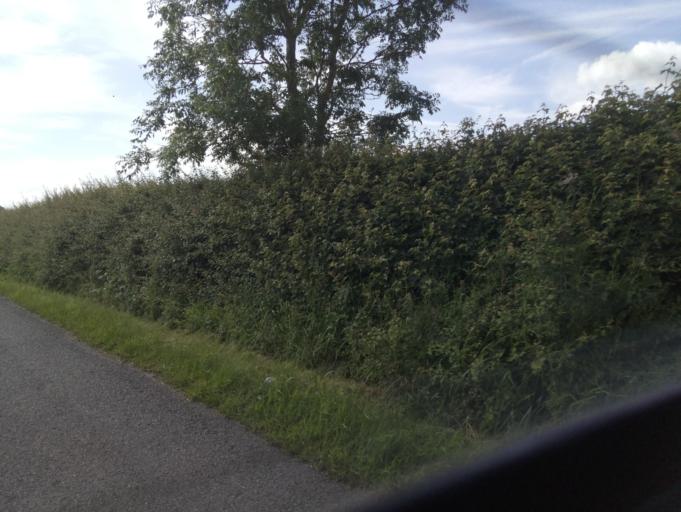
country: GB
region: England
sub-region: Lincolnshire
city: Skellingthorpe
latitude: 53.1472
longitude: -0.6322
